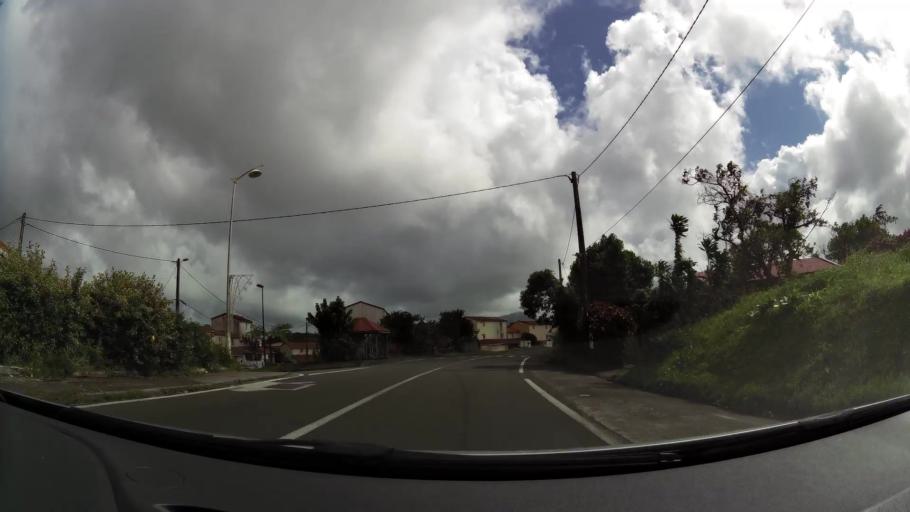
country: MQ
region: Martinique
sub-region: Martinique
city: Le Morne-Rouge
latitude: 14.7858
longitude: -61.1380
